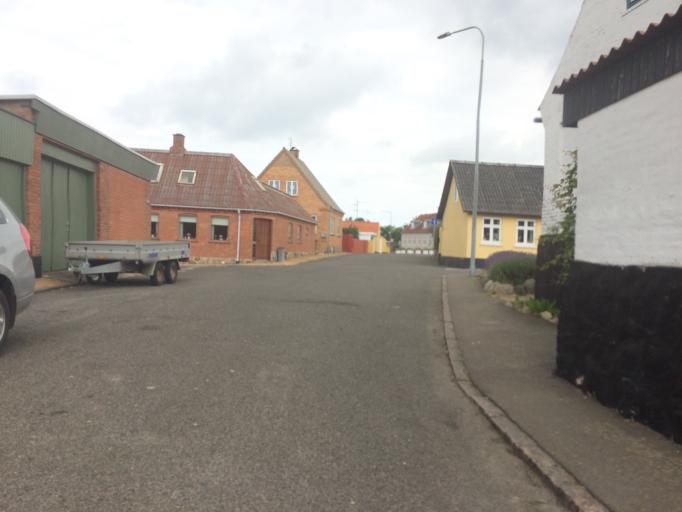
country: DK
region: Capital Region
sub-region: Bornholm Kommune
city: Ronne
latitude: 55.1864
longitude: 14.7071
